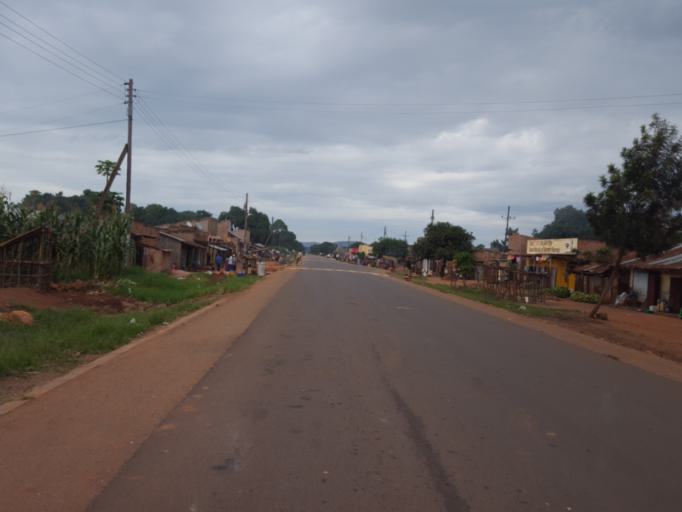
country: UG
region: Central Region
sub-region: Kiboga District
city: Kiboga
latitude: 1.0307
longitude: 31.6786
